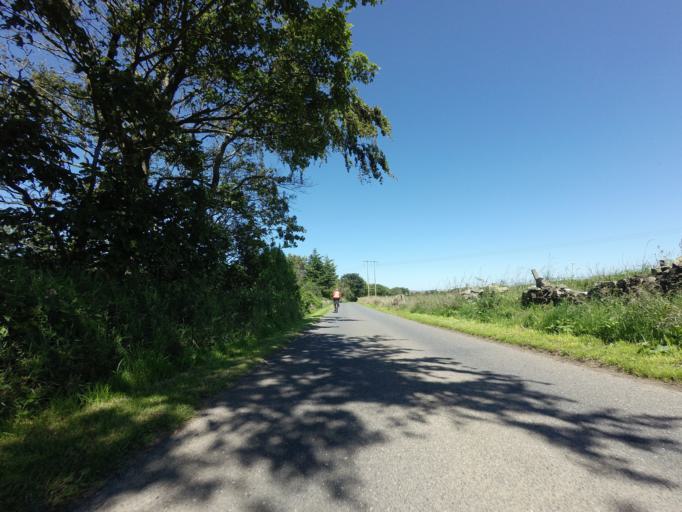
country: GB
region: Scotland
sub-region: Aberdeenshire
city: Macduff
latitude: 57.6577
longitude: -2.4984
